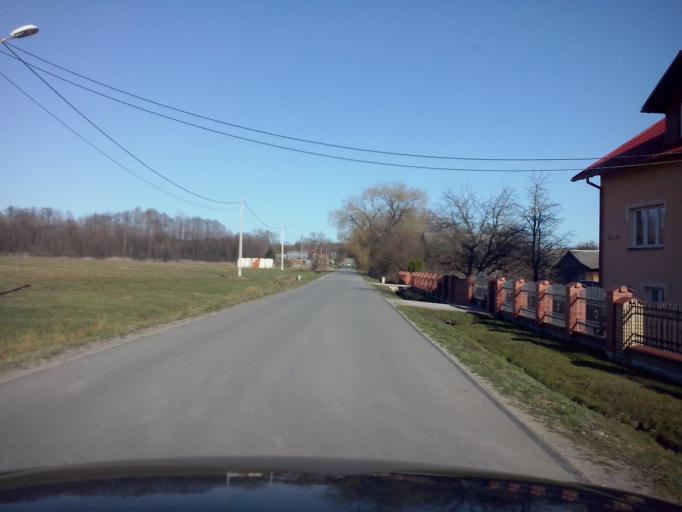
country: PL
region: Subcarpathian Voivodeship
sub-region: Powiat nizanski
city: Krzeszow
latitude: 50.3939
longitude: 22.3911
